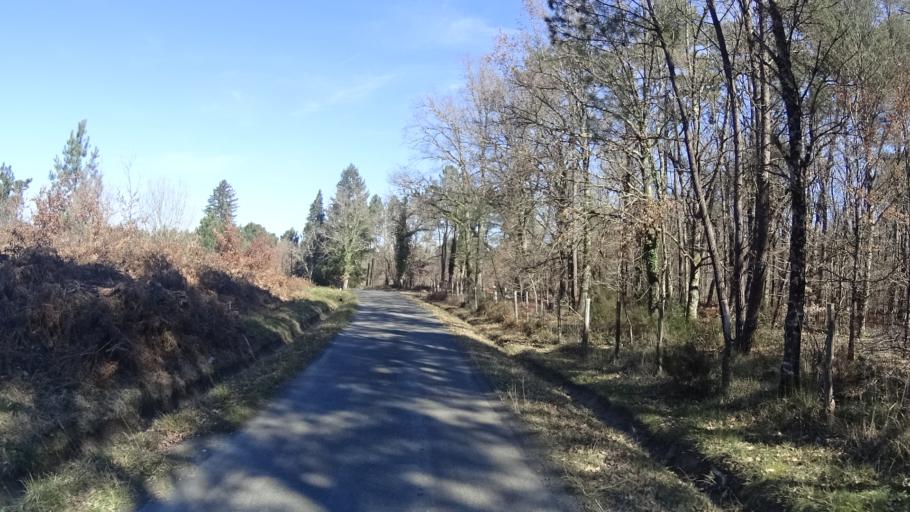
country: FR
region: Aquitaine
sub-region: Departement de la Dordogne
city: Riberac
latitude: 45.1847
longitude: 0.3035
